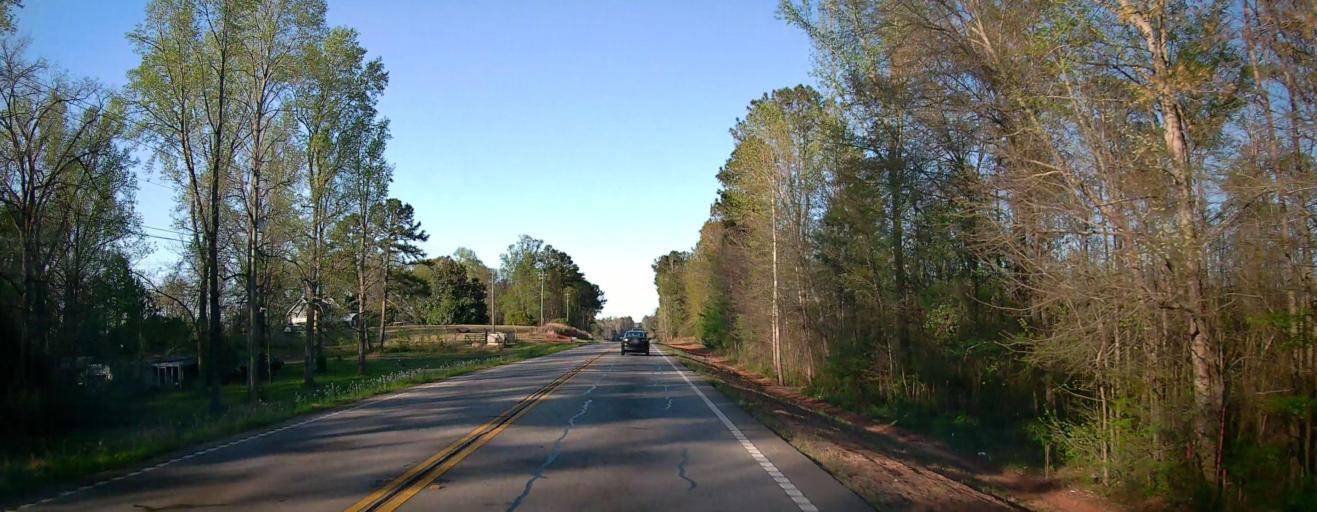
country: US
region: Georgia
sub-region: Butts County
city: Jackson
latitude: 33.3888
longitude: -83.8990
